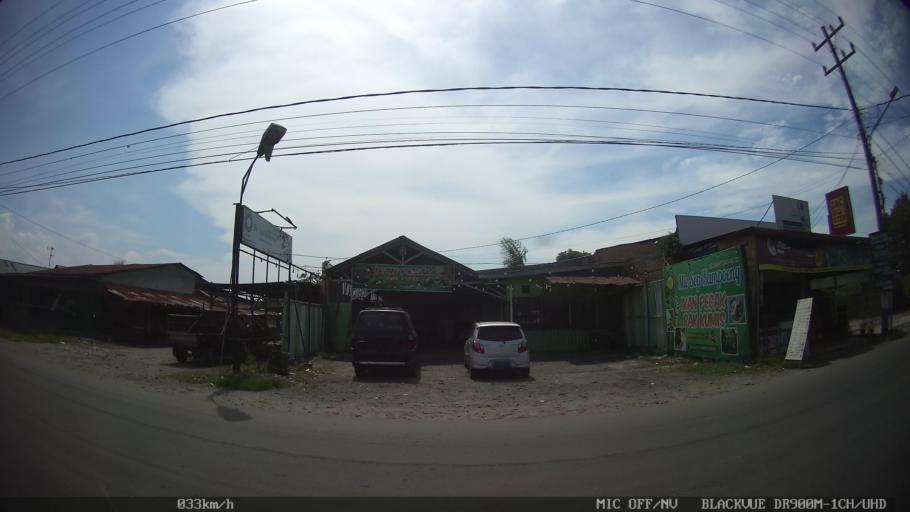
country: ID
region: North Sumatra
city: Labuhan Deli
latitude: 3.6714
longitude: 98.6558
